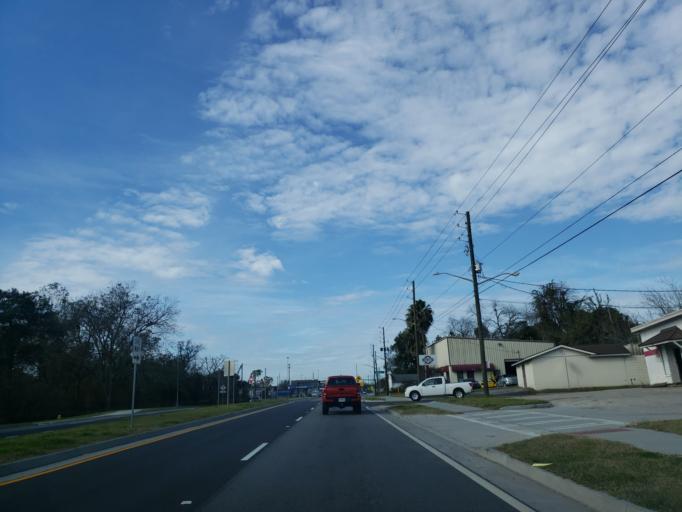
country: US
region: Georgia
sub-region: Chatham County
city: Savannah
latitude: 32.0891
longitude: -81.1212
